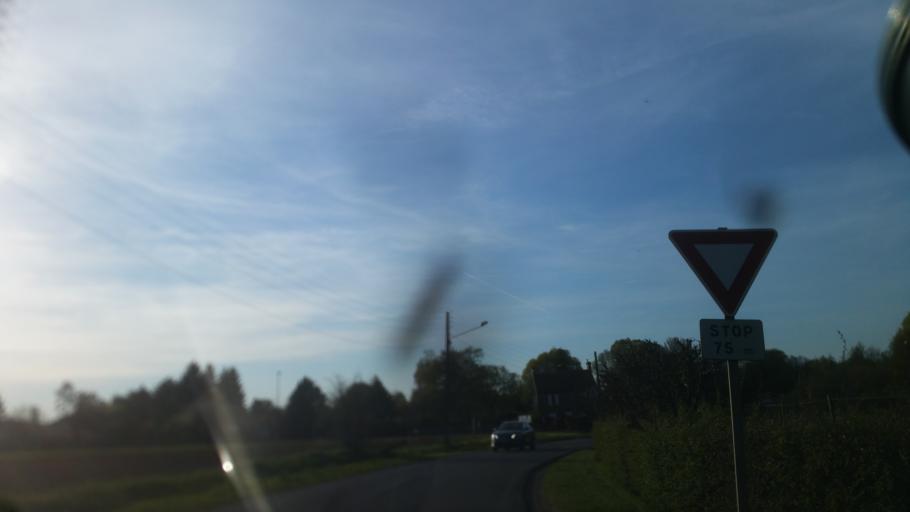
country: FR
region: Ile-de-France
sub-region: Departement de l'Essonne
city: Saint-Cyr-sous-Dourdan
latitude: 48.5674
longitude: 2.0325
